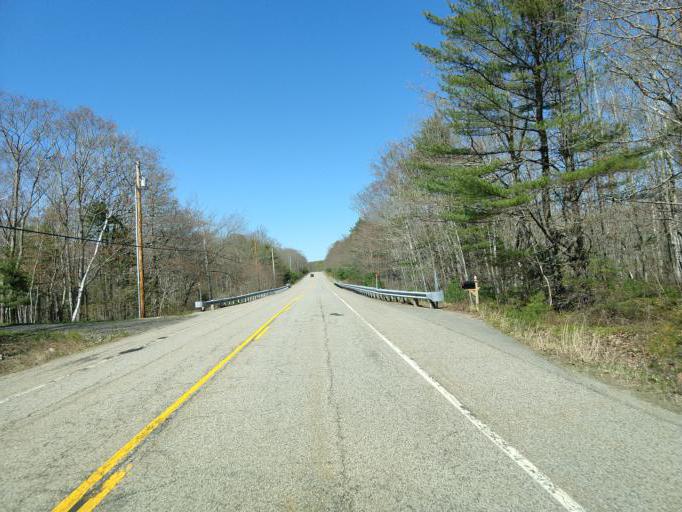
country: US
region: Maine
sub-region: York County
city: Old Orchard Beach
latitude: 43.4294
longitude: -70.3825
